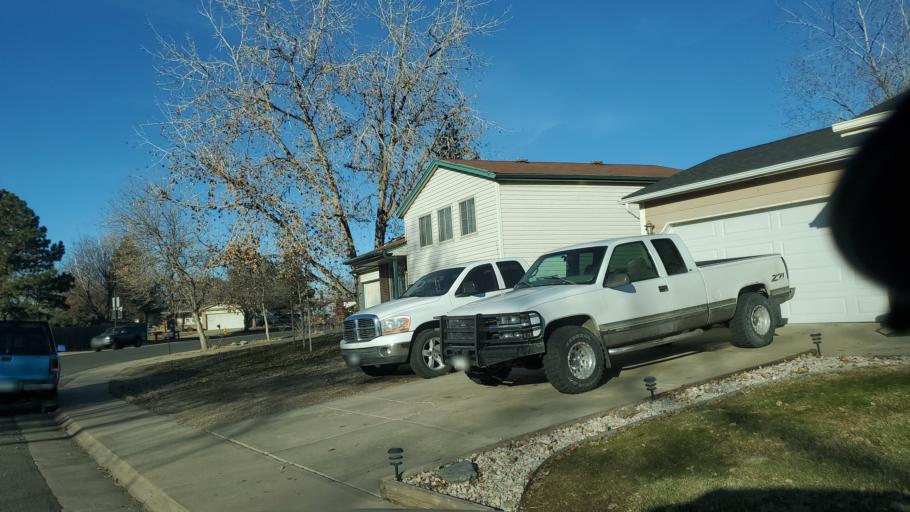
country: US
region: Colorado
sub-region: Adams County
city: Thornton
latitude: 39.9071
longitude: -104.9384
